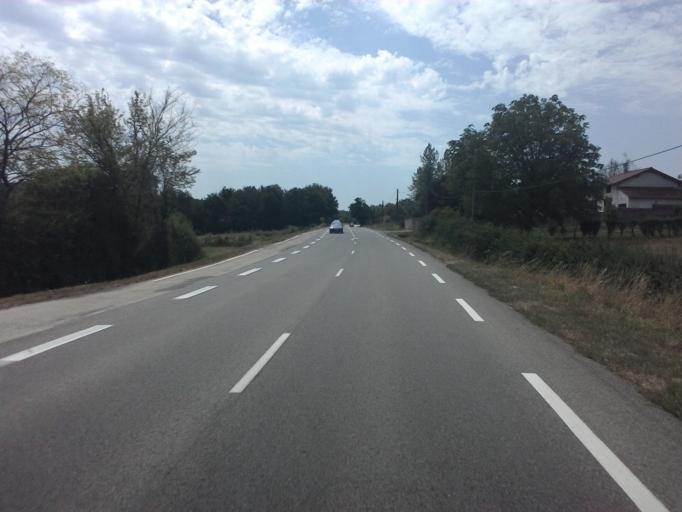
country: FR
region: Rhone-Alpes
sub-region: Departement de l'Ain
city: Saint-Etienne-du-Bois
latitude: 46.3212
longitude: 5.3072
